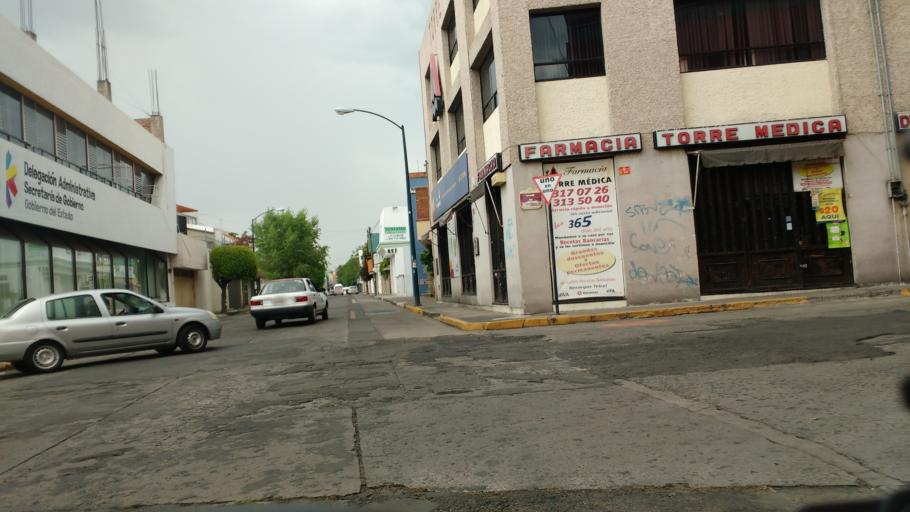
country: MX
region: Michoacan
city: Morelia
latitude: 19.6965
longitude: -101.1836
